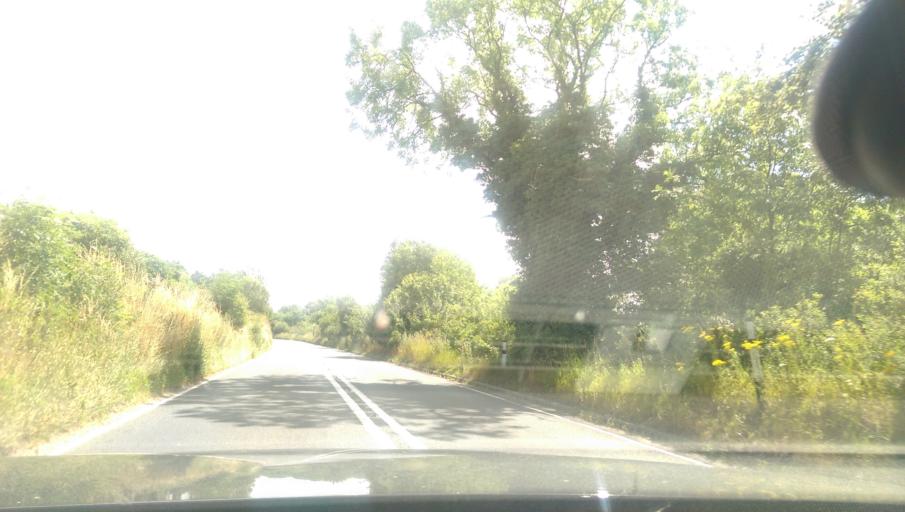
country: GB
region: England
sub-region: Wiltshire
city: Stapleford
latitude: 51.1320
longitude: -1.9108
